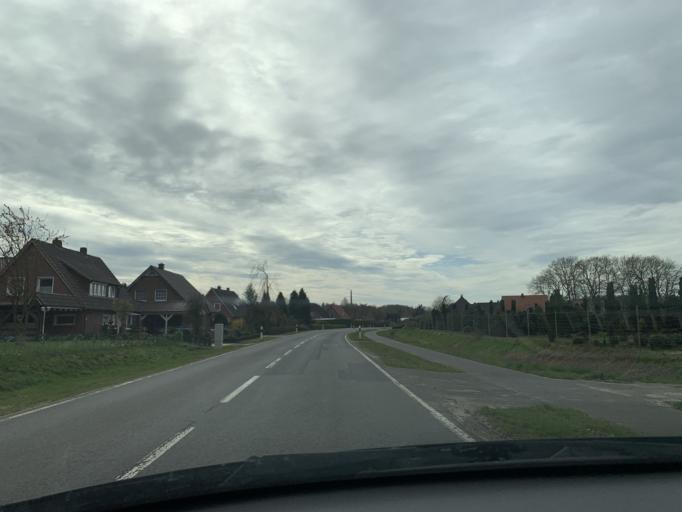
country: DE
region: Lower Saxony
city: Edewecht
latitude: 53.1568
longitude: 7.9740
